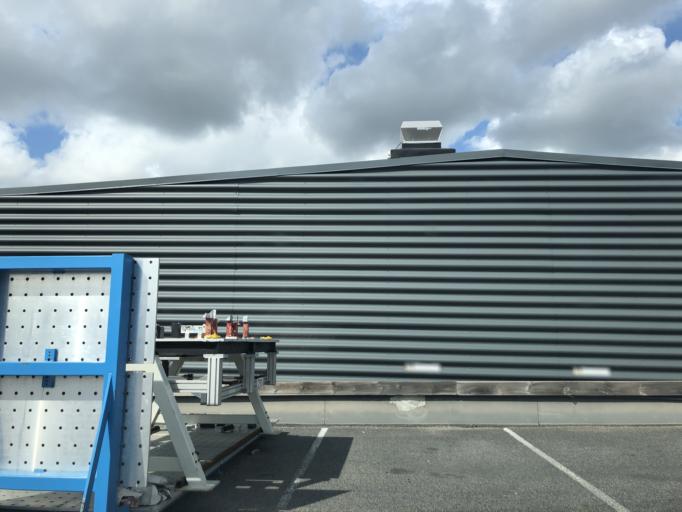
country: SE
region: Vaestra Goetaland
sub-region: Goteborg
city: Majorna
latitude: 57.7060
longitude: 11.8833
